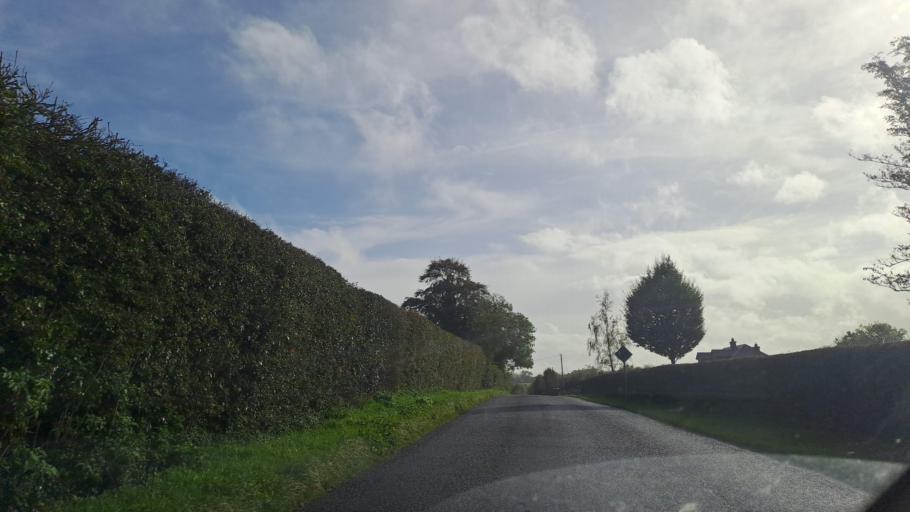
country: IE
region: Ulster
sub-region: County Monaghan
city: Carrickmacross
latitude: 53.8888
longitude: -6.6939
